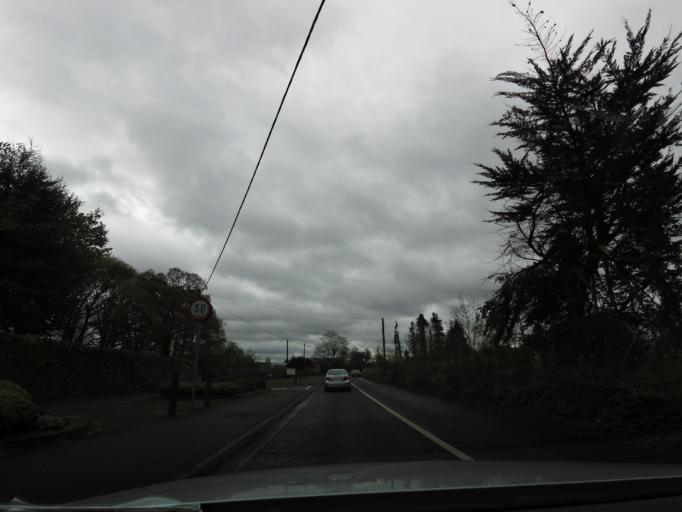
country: IE
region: Leinster
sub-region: Kilkenny
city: Kilkenny
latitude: 52.6716
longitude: -7.2676
